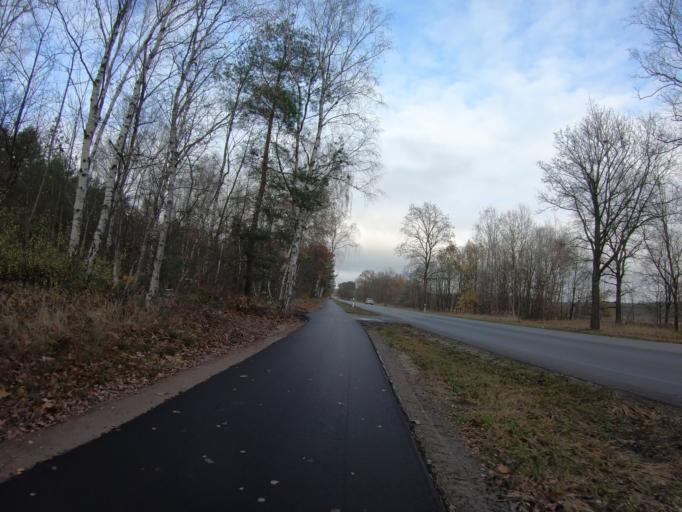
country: DE
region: Lower Saxony
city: Wagenhoff
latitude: 52.5654
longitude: 10.5184
